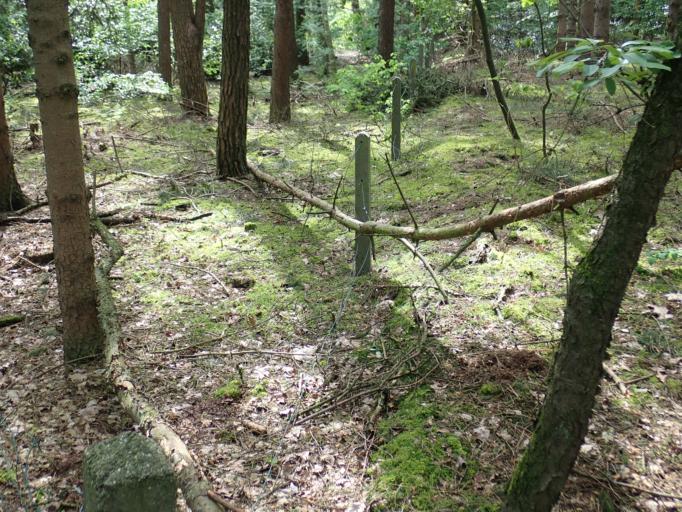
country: BE
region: Flanders
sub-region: Provincie Antwerpen
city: Lille
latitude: 51.2395
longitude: 4.8336
